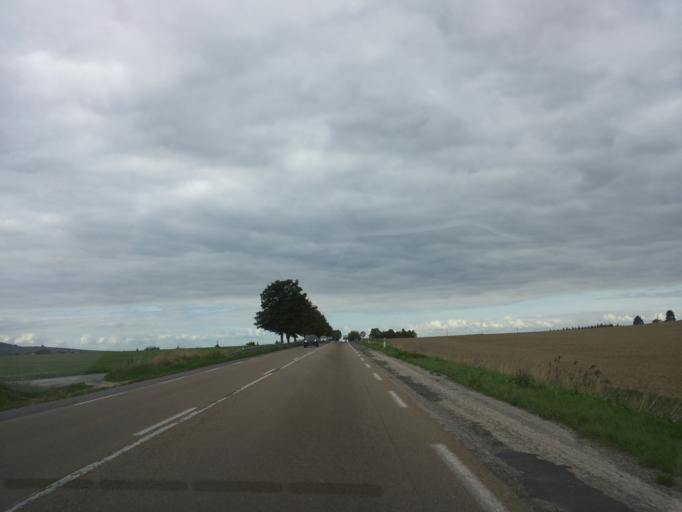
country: FR
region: Champagne-Ardenne
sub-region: Departement de la Marne
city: Verzy
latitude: 49.1299
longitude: 4.2362
